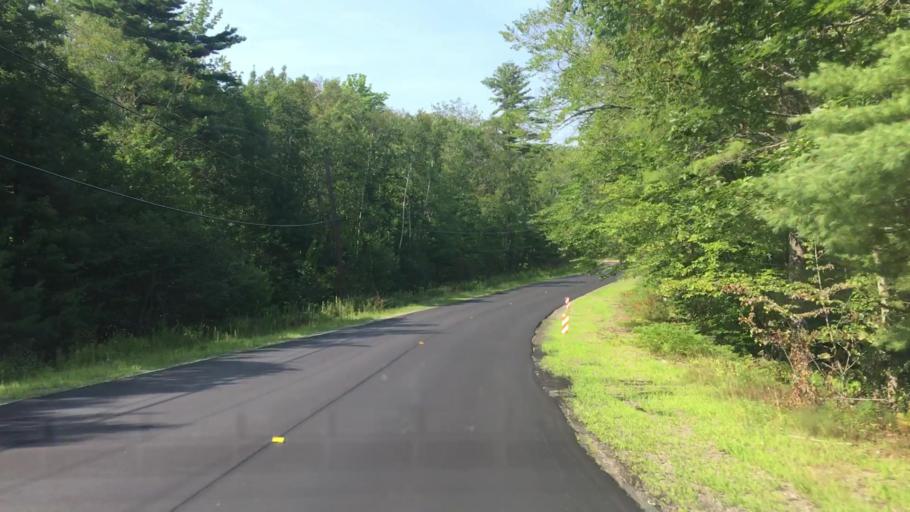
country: US
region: Maine
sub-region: Sagadahoc County
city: Woolwich
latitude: 43.9299
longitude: -69.8010
